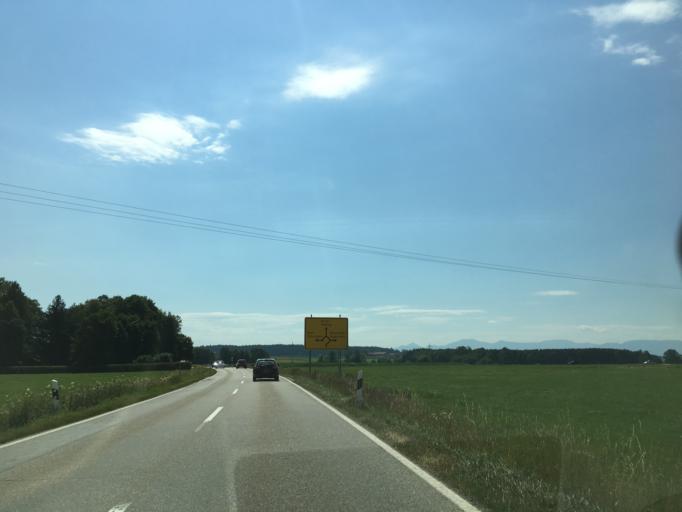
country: DE
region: Bavaria
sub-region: Upper Bavaria
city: Schonstett
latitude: 47.9748
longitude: 12.2281
